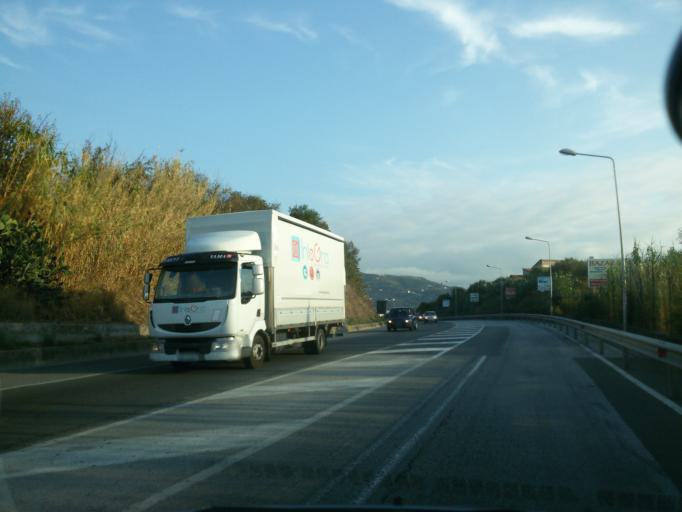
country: IT
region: Liguria
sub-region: Provincia di Savona
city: Valleggia
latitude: 44.2902
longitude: 8.4500
